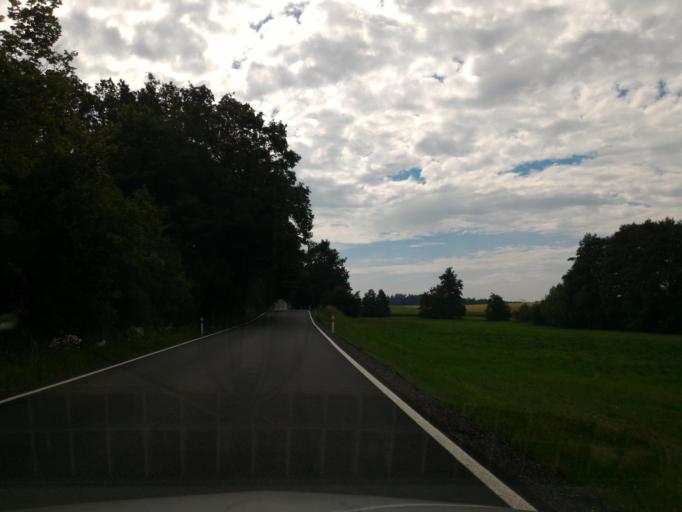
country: CZ
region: Vysocina
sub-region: Okres Jihlava
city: Telc
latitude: 49.1622
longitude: 15.5077
